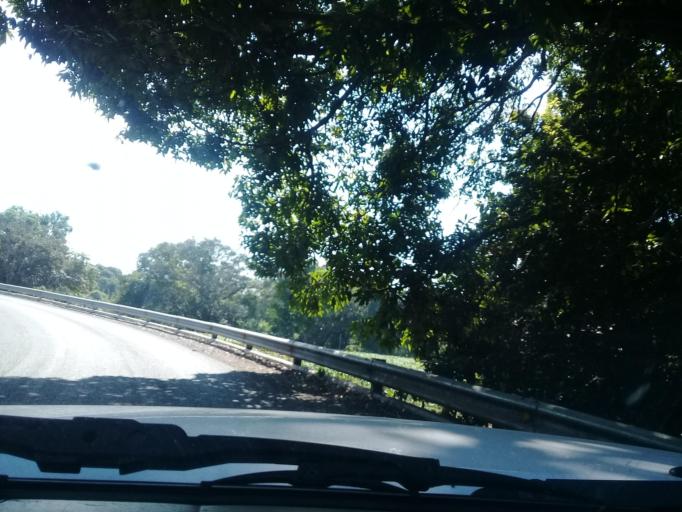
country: MX
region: Veracruz
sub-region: Emiliano Zapata
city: Plan del Rio
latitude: 19.4196
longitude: -96.6173
